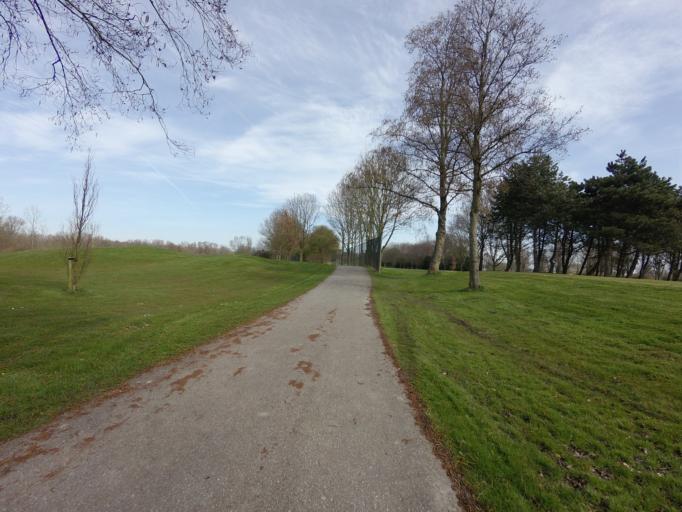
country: NL
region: South Holland
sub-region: Gemeente Alphen aan den Rijn
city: Alphen aan den Rijn
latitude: 52.1383
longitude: 4.6923
